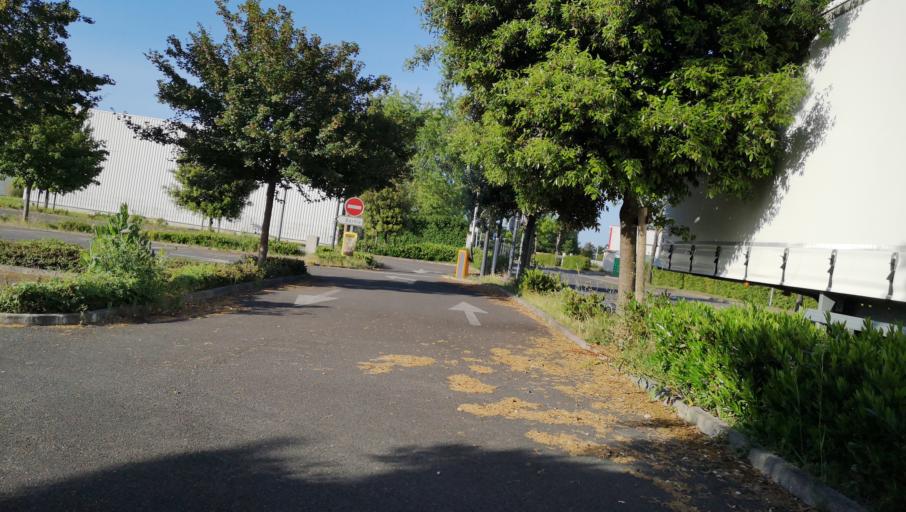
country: FR
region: Centre
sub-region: Departement du Loiret
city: Semoy
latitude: 47.9112
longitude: 1.9437
